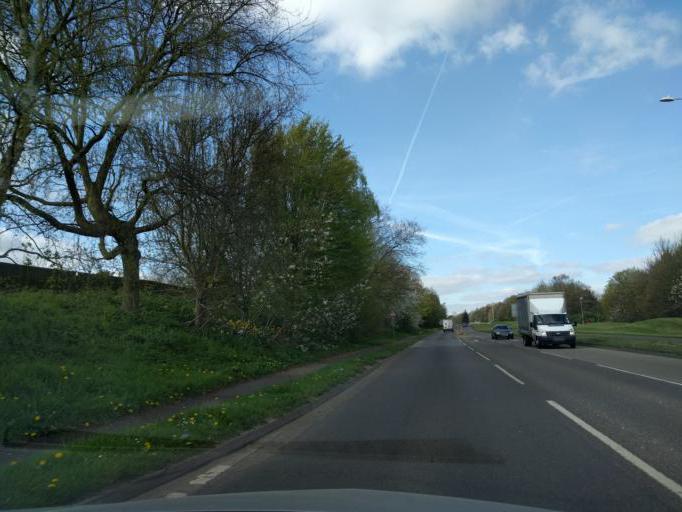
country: GB
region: England
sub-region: Northamptonshire
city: Earls Barton
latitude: 52.2548
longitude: -0.8096
